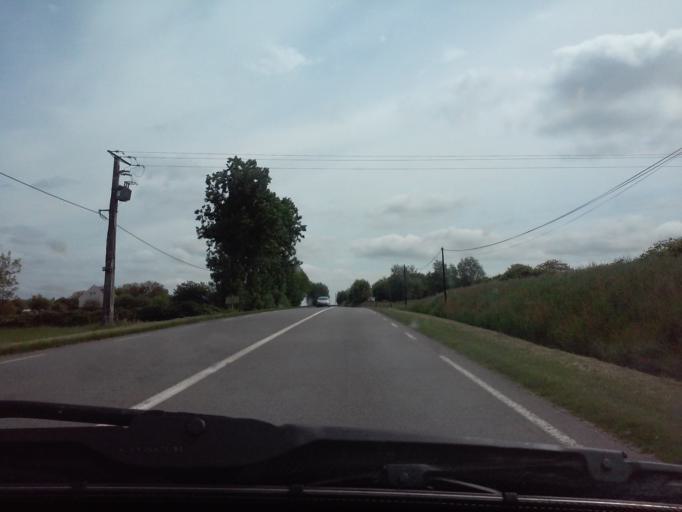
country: FR
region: Brittany
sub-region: Departement d'Ille-et-Vilaine
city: Fougeres
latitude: 48.3360
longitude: -1.1884
